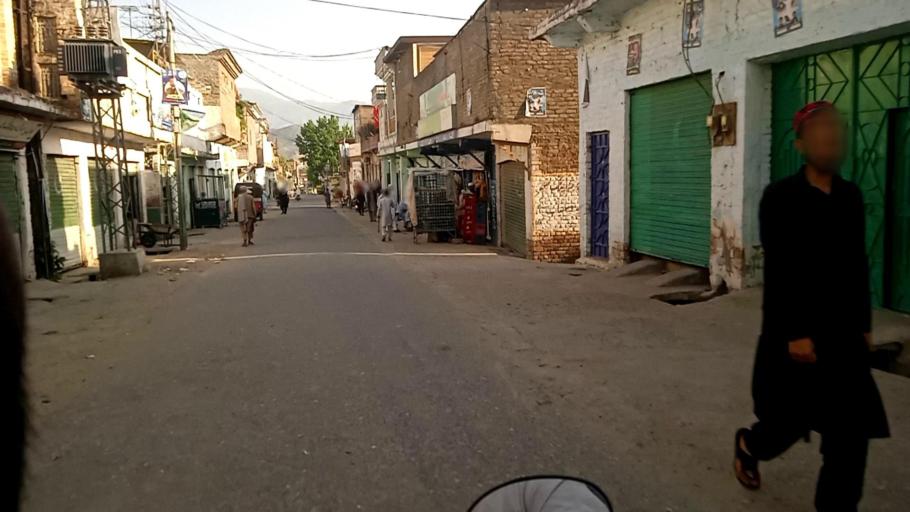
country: PK
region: Khyber Pakhtunkhwa
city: Mingora
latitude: 34.8130
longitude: 72.3595
